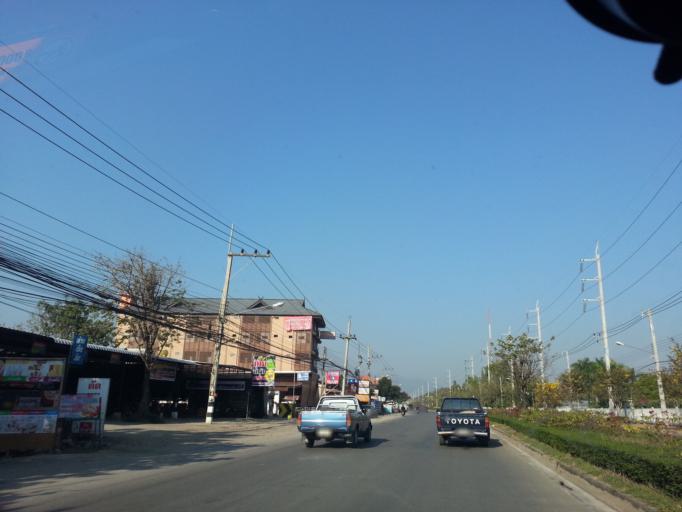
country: TH
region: Chiang Mai
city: San Sai
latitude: 18.8910
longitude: 99.0203
